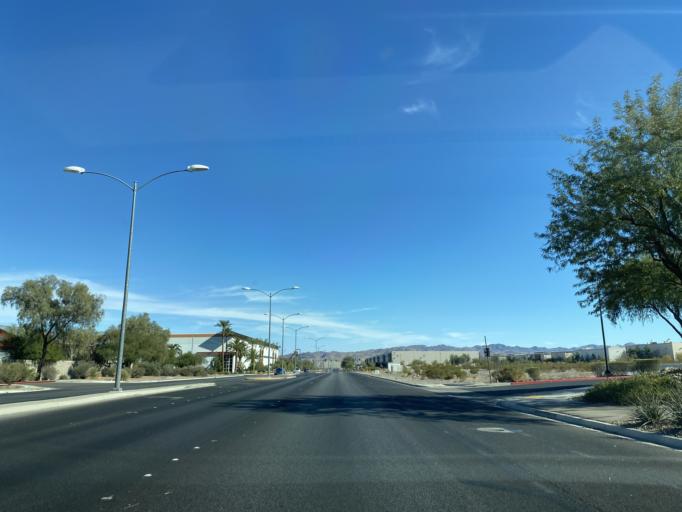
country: US
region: Nevada
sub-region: Clark County
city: Henderson
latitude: 36.0563
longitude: -115.0239
